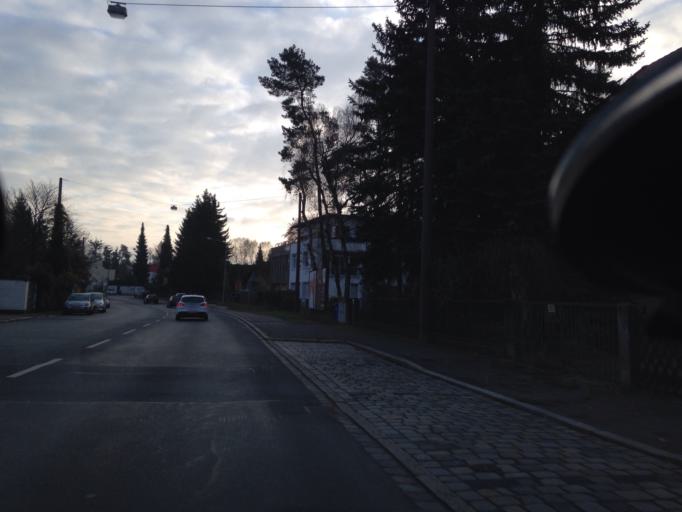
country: DE
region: Bavaria
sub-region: Regierungsbezirk Mittelfranken
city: Schwaig
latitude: 49.4689
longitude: 11.1759
